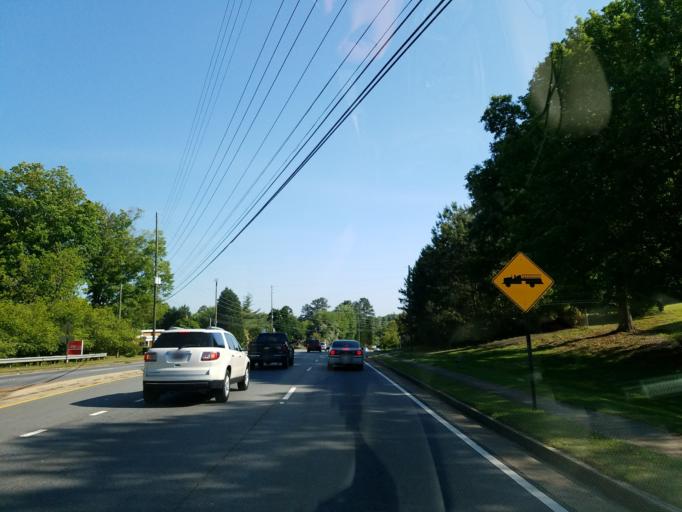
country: US
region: Georgia
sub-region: Cobb County
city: Kennesaw
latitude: 33.9524
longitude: -84.6231
